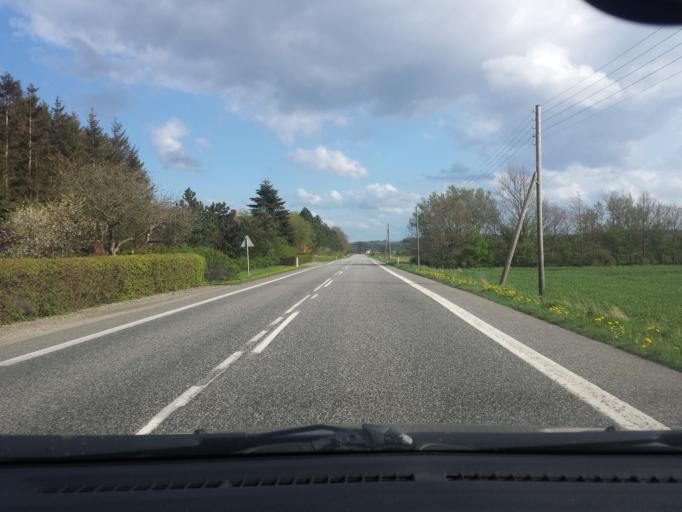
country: DK
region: Central Jutland
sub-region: Favrskov Kommune
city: Ulstrup
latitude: 56.4600
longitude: 9.7451
